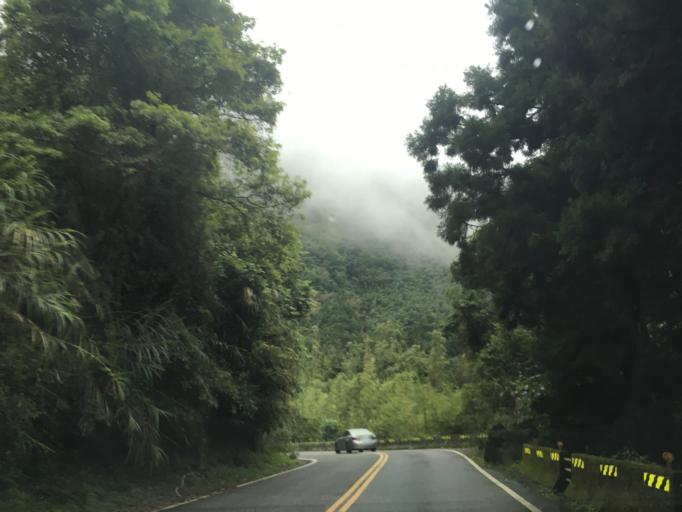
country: TW
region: Taiwan
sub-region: Chiayi
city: Jiayi Shi
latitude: 23.4983
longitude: 120.7013
